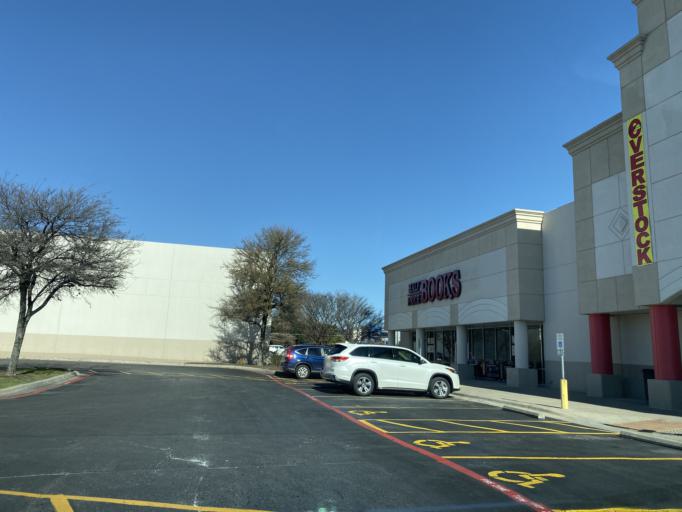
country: US
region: Texas
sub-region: Williamson County
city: Round Rock
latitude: 30.4848
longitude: -97.6710
